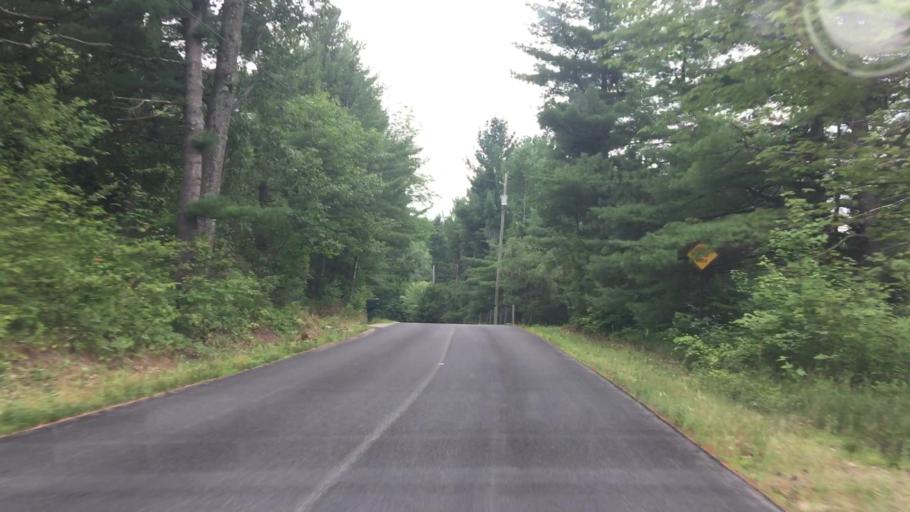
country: US
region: New York
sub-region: Essex County
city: Keeseville
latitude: 44.4210
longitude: -73.6356
